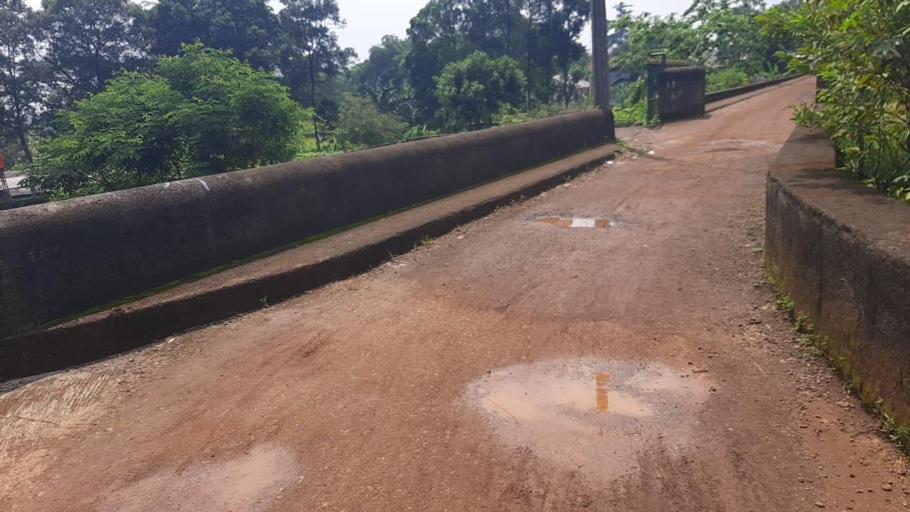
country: ID
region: West Java
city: Cileungsir
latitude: -6.4195
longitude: 106.9149
